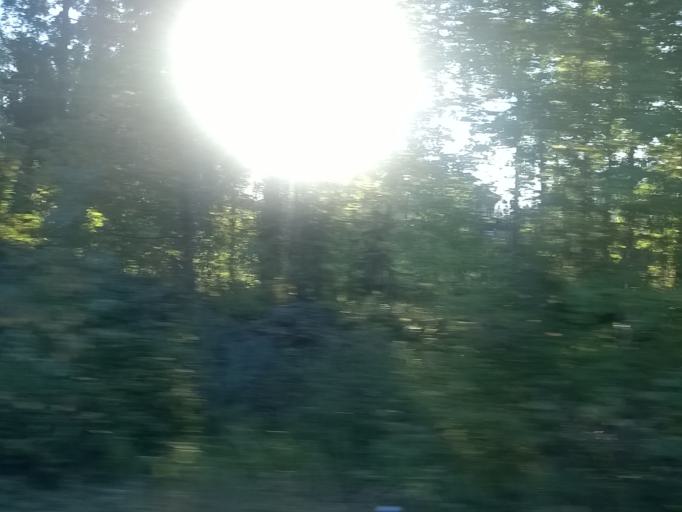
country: FI
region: Pirkanmaa
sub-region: Tampere
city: Tampere
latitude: 61.4368
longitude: 23.8472
